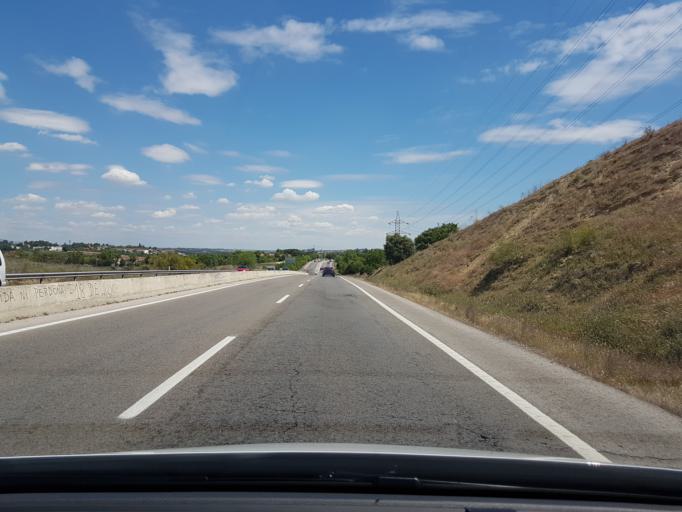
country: ES
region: Madrid
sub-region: Provincia de Madrid
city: Moncloa-Aravaca
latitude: 40.4442
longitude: -3.7710
